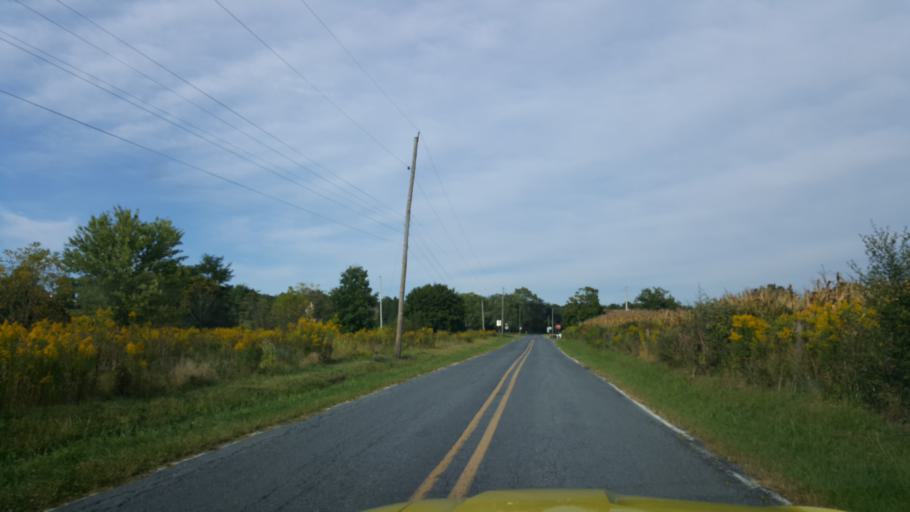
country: US
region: Pennsylvania
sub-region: Lebanon County
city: Campbelltown
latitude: 40.2425
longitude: -76.5644
